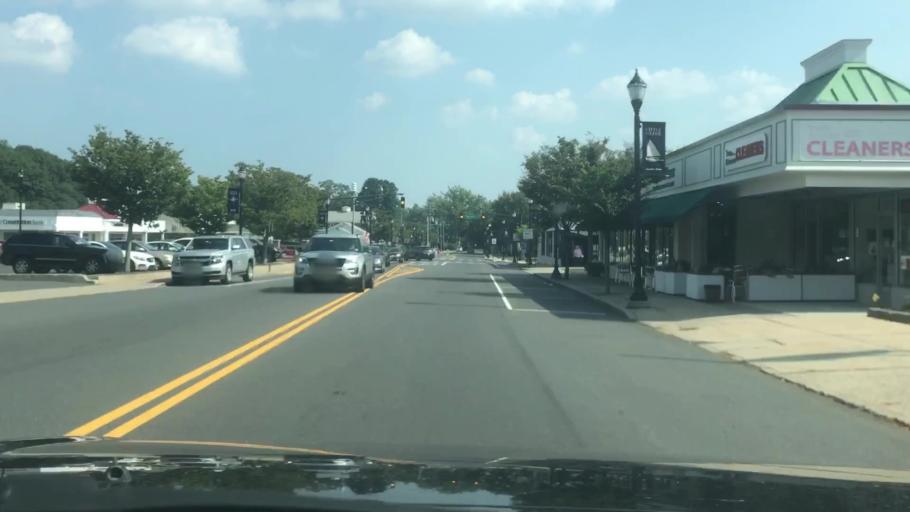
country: US
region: New Jersey
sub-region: Monmouth County
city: Little Silver
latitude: 40.3390
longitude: -74.0420
